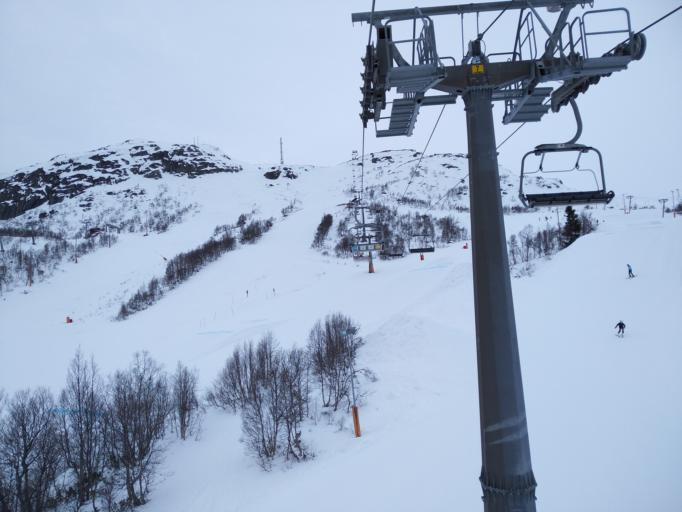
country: NO
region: Aust-Agder
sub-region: Bykle
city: Hovden
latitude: 59.5743
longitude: 7.3409
